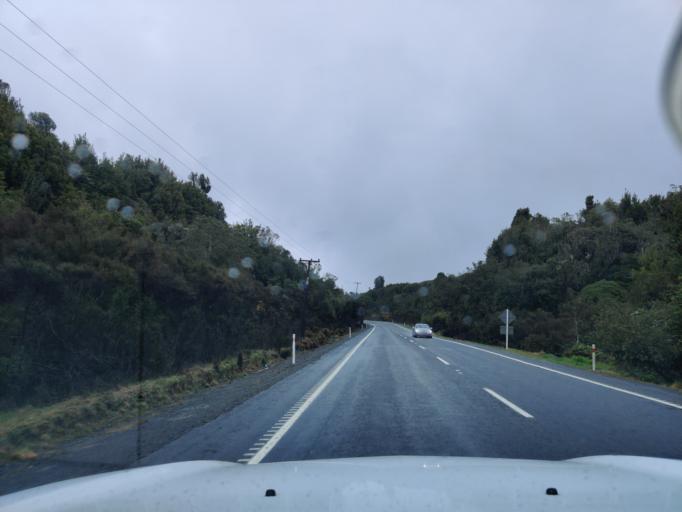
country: NZ
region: Bay of Plenty
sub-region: Rotorua District
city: Rotorua
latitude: -38.0360
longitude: 176.0401
